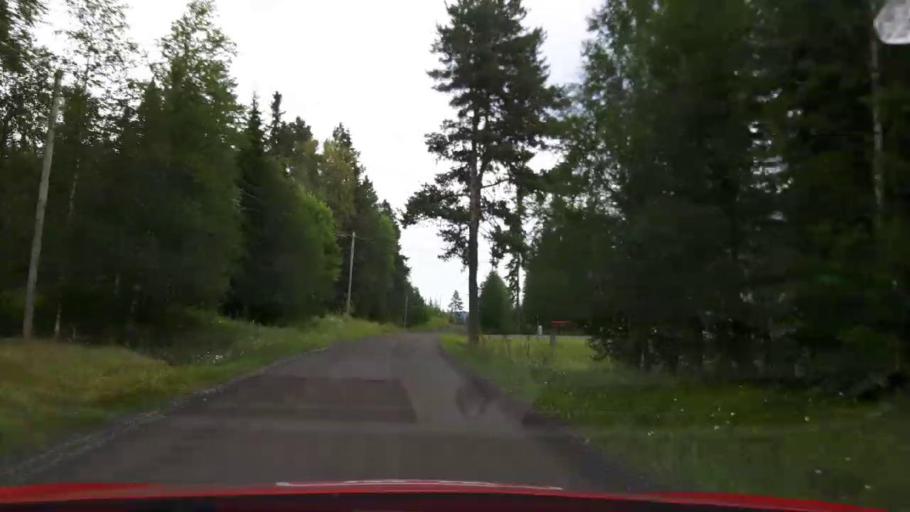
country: SE
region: Jaemtland
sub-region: OEstersunds Kommun
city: Lit
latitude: 63.4477
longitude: 15.2719
